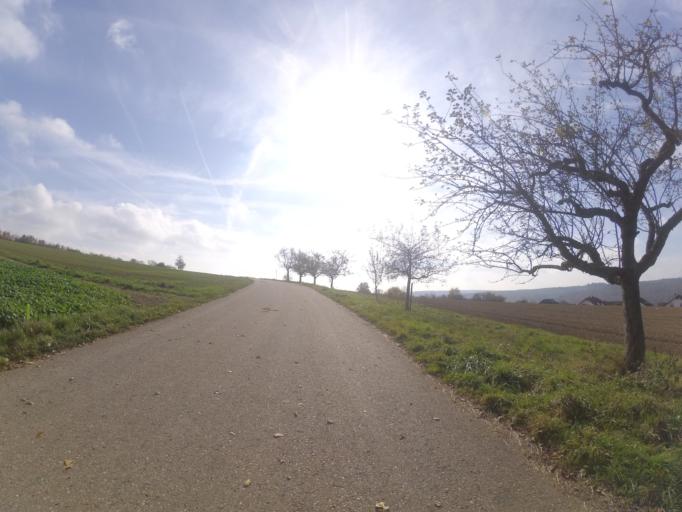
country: DE
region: Baden-Wuerttemberg
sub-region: Tuebingen Region
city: Dornstadt
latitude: 48.4187
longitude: 9.9295
